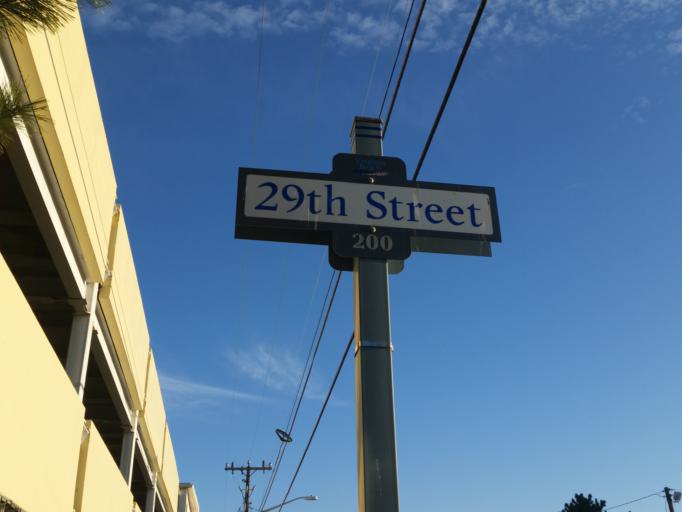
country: US
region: Virginia
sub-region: City of Virginia Beach
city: Virginia Beach
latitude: 36.8571
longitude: -75.9786
